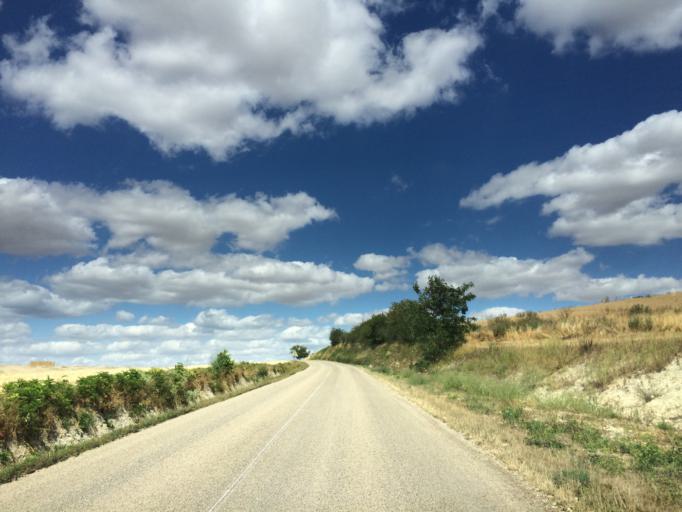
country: FR
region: Bourgogne
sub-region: Departement de l'Yonne
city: Laroche-Saint-Cydroine
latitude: 47.9182
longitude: 3.4704
